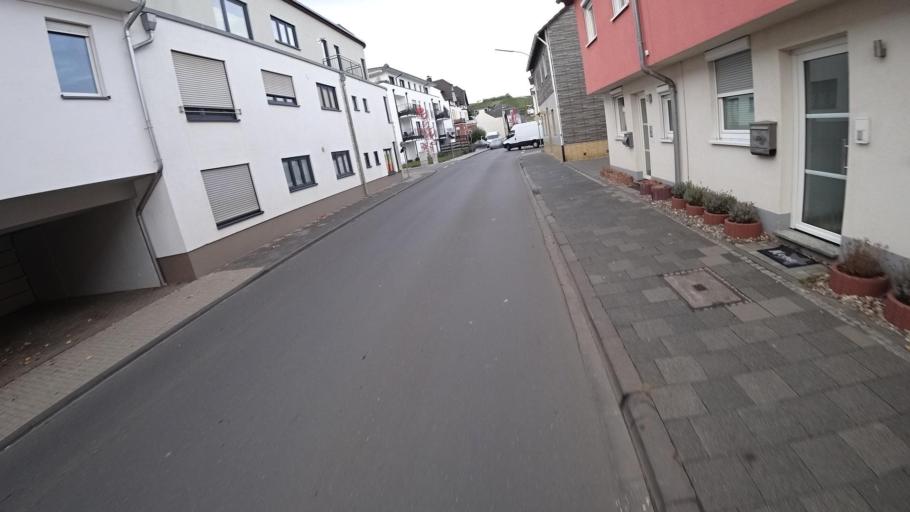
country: DE
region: Rheinland-Pfalz
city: Bad Neuenahr-Ahrweiler
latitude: 50.5453
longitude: 7.1447
